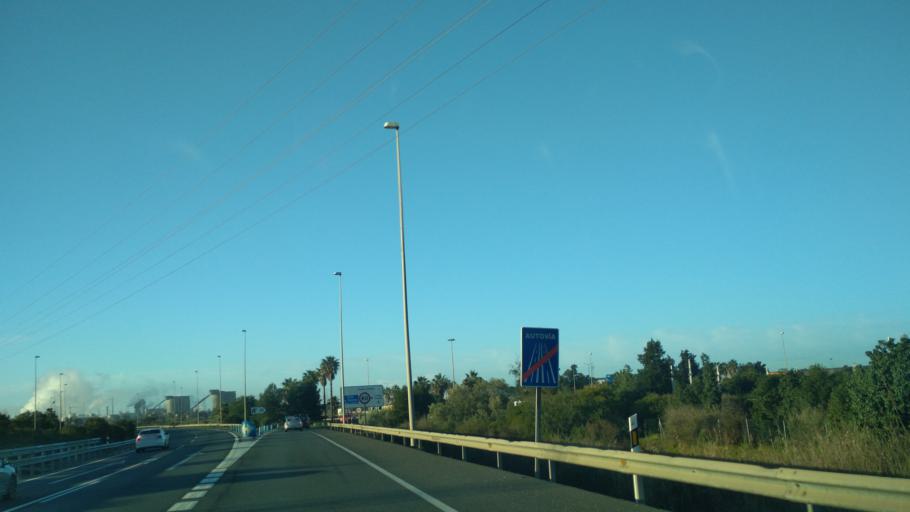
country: ES
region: Andalusia
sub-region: Provincia de Huelva
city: Huelva
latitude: 37.2451
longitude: -6.9441
